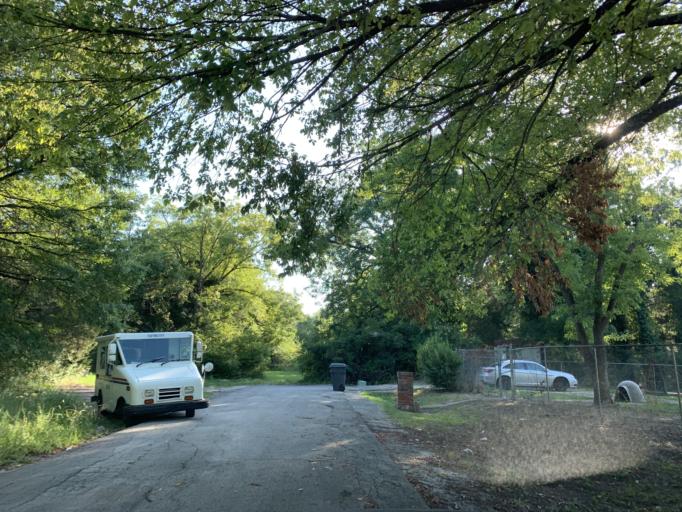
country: US
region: Texas
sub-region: Dallas County
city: Hutchins
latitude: 32.6701
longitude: -96.7743
